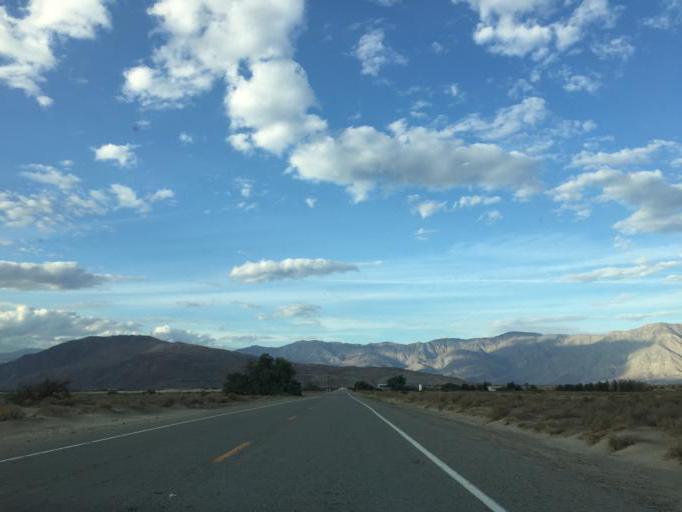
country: US
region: California
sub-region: San Diego County
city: Borrego Springs
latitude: 33.2663
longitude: -116.2988
